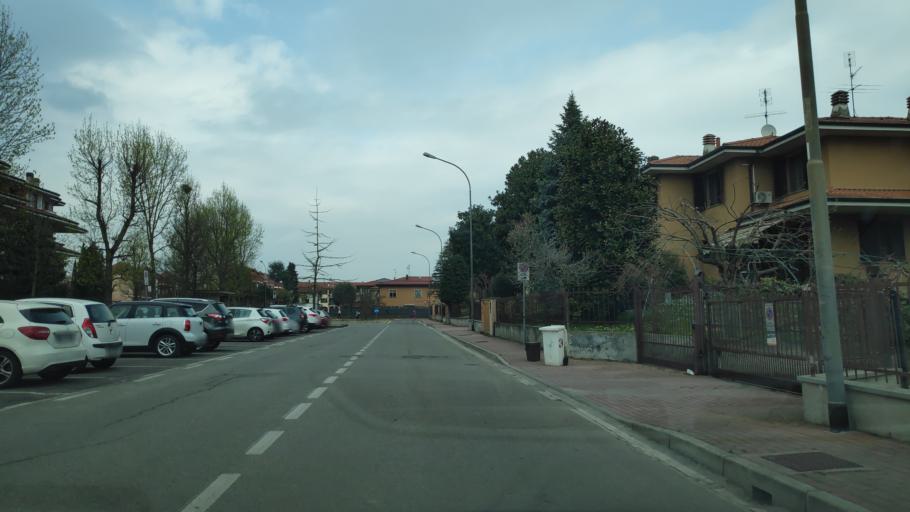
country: IT
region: Lombardy
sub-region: Citta metropolitana di Milano
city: Liscate
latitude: 45.4791
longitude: 9.4083
